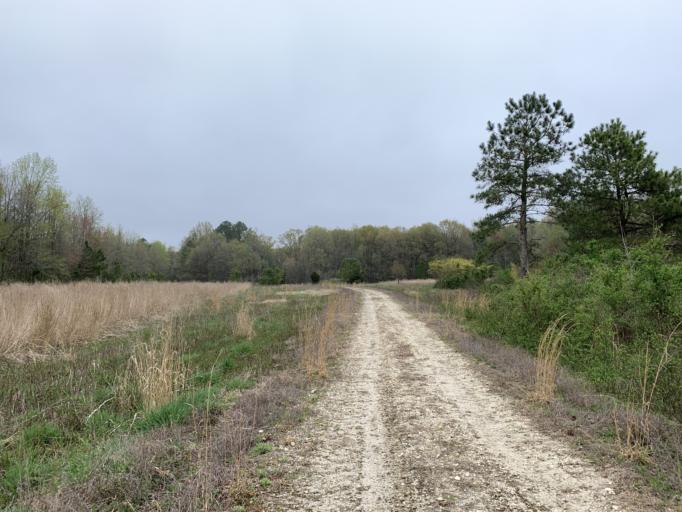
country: US
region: Delaware
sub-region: Kent County
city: Felton
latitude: 39.0210
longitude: -75.6349
